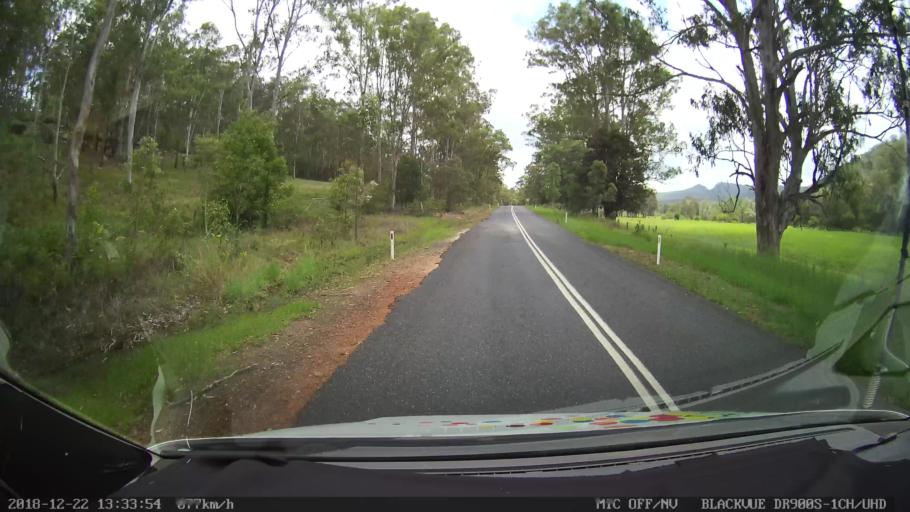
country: AU
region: New South Wales
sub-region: Clarence Valley
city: Coutts Crossing
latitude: -29.8663
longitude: 152.8232
